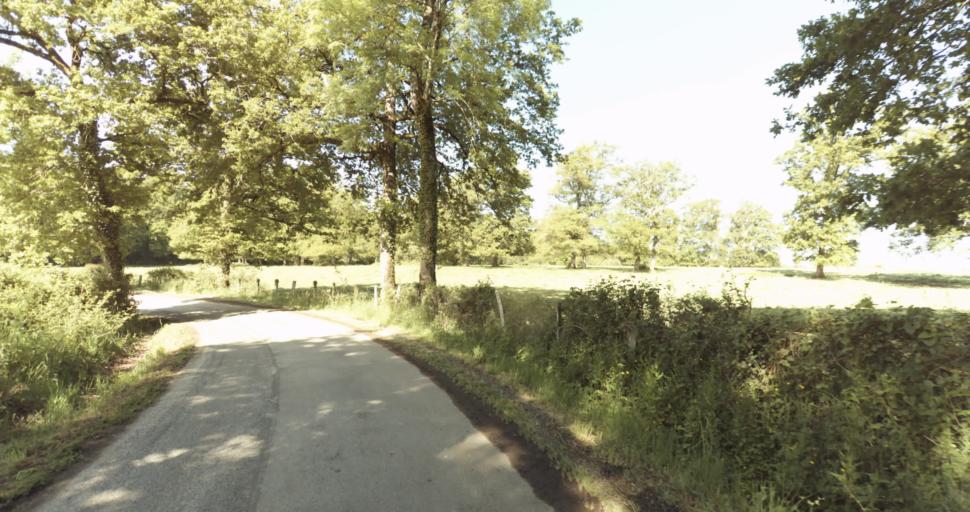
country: FR
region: Limousin
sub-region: Departement de la Haute-Vienne
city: Solignac
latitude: 45.7010
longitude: 1.2552
